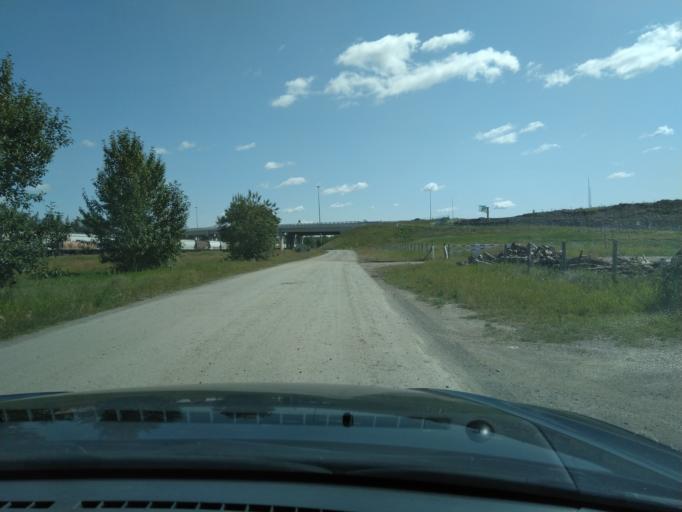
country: CA
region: Alberta
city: Calgary
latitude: 51.1022
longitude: -114.2326
